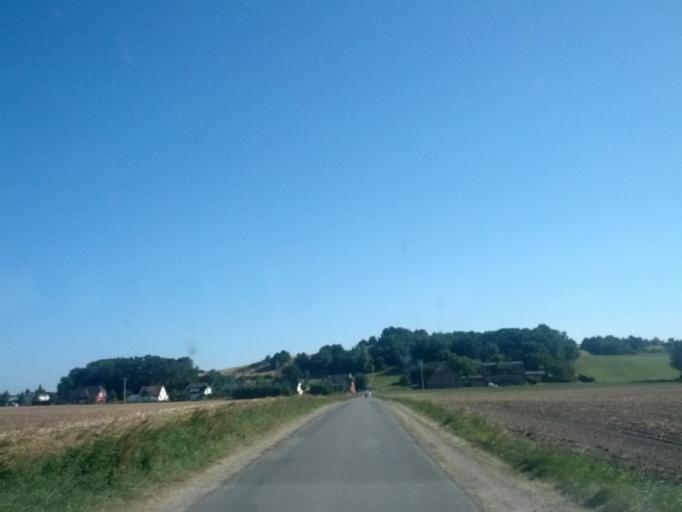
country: DE
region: Mecklenburg-Vorpommern
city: Ostseebad Sellin
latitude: 54.3330
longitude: 13.6879
